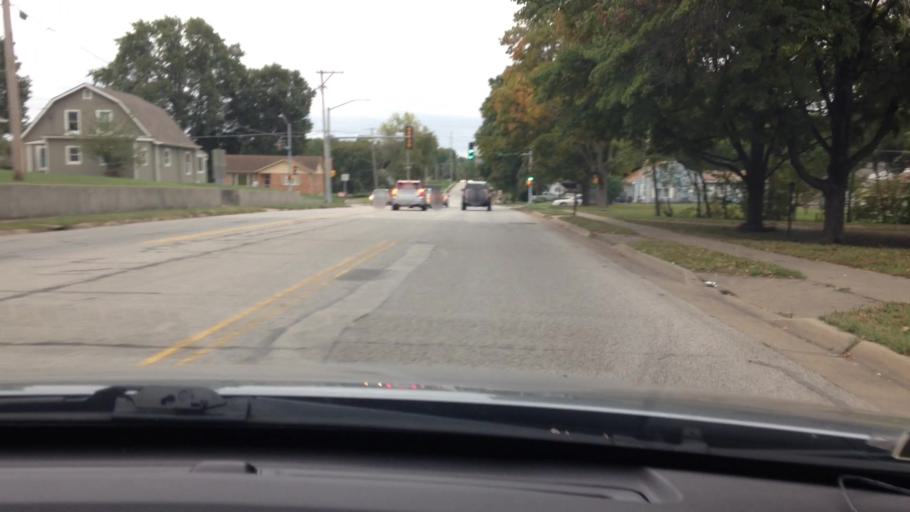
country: US
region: Kansas
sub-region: Leavenworth County
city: Leavenworth
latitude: 39.2895
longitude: -94.9278
